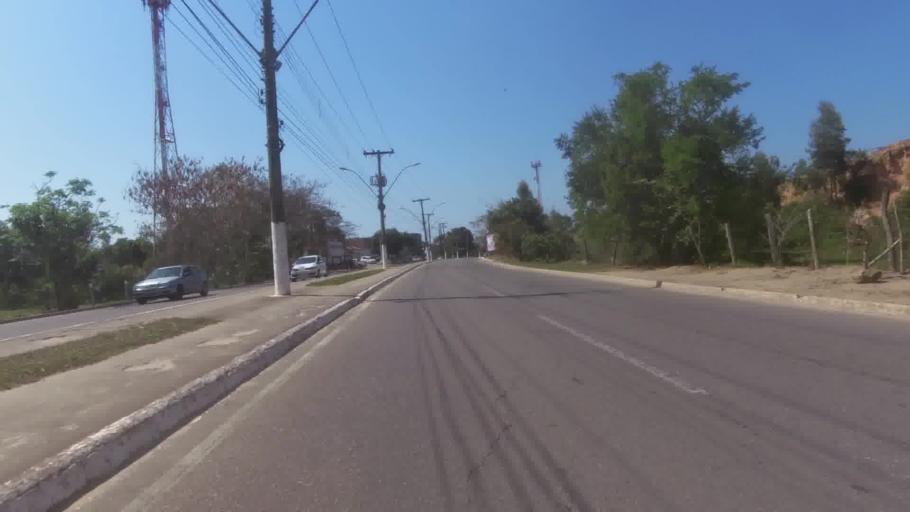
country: BR
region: Espirito Santo
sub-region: Itapemirim
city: Itapemirim
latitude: -21.0092
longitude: -40.8231
